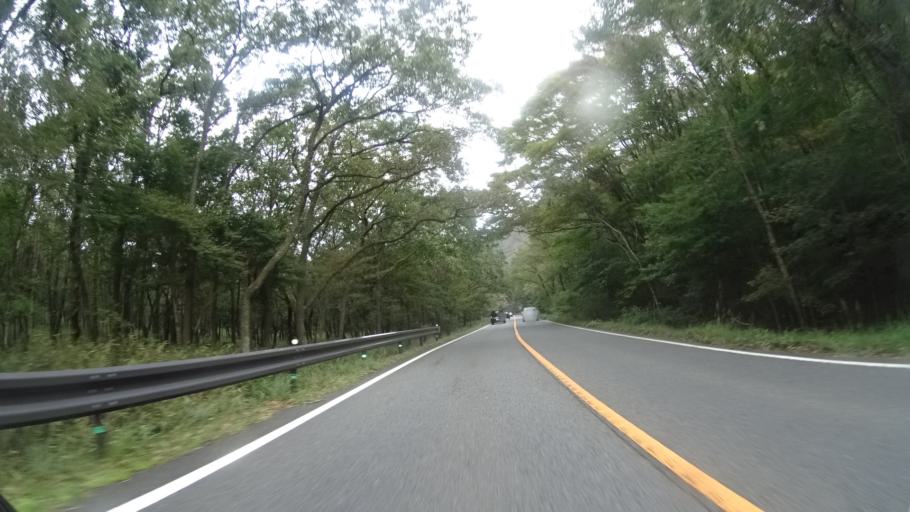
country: JP
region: Oita
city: Beppu
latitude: 33.2680
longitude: 131.4031
